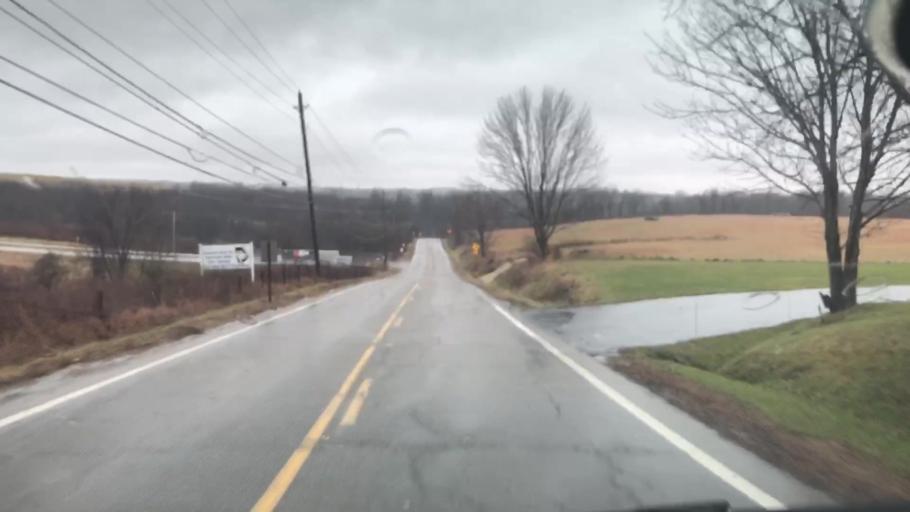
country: US
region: Ohio
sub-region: Harrison County
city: Cadiz
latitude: 40.2667
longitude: -81.0002
